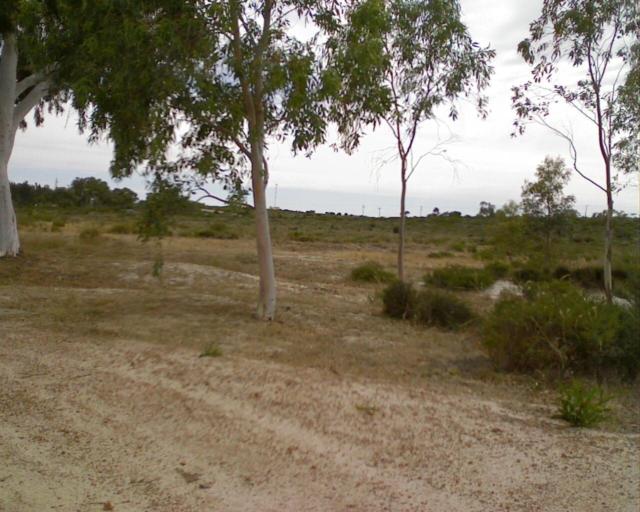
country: AU
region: Western Australia
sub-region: Dandaragan
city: Jurien Bay
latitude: -29.8224
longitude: 115.2735
